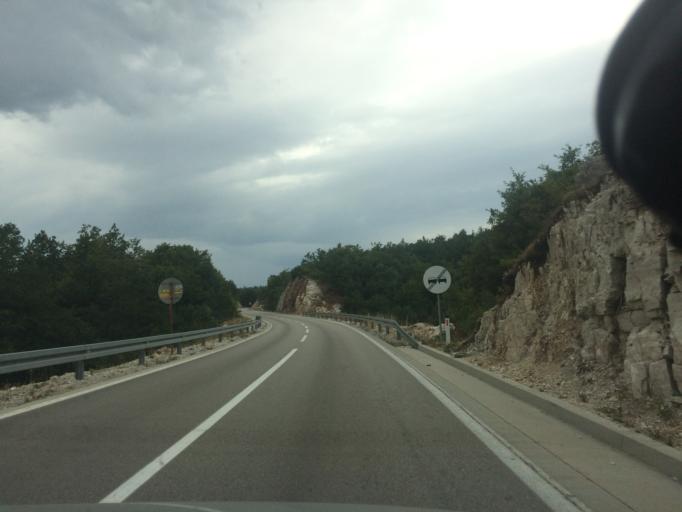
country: ME
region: Kotor
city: Risan
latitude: 42.7063
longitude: 18.6128
